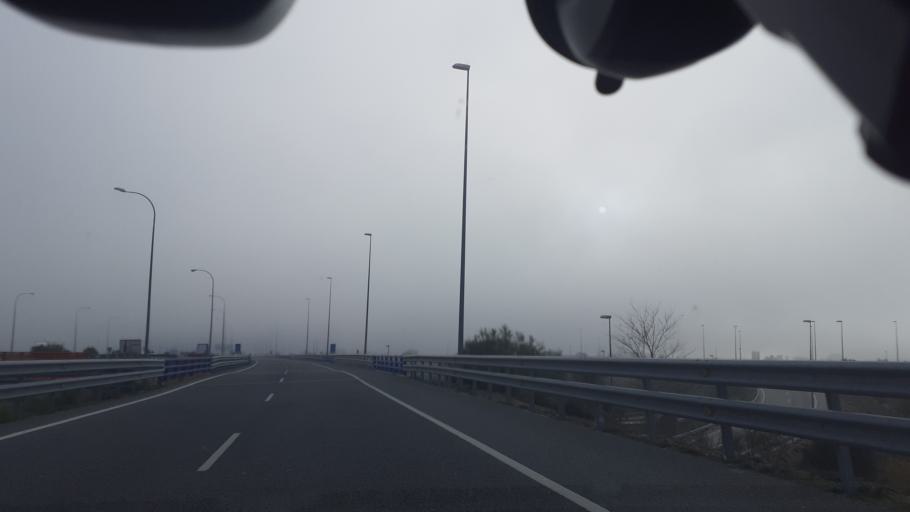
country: ES
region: Madrid
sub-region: Provincia de Madrid
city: Coslada
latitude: 40.4036
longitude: -3.5725
